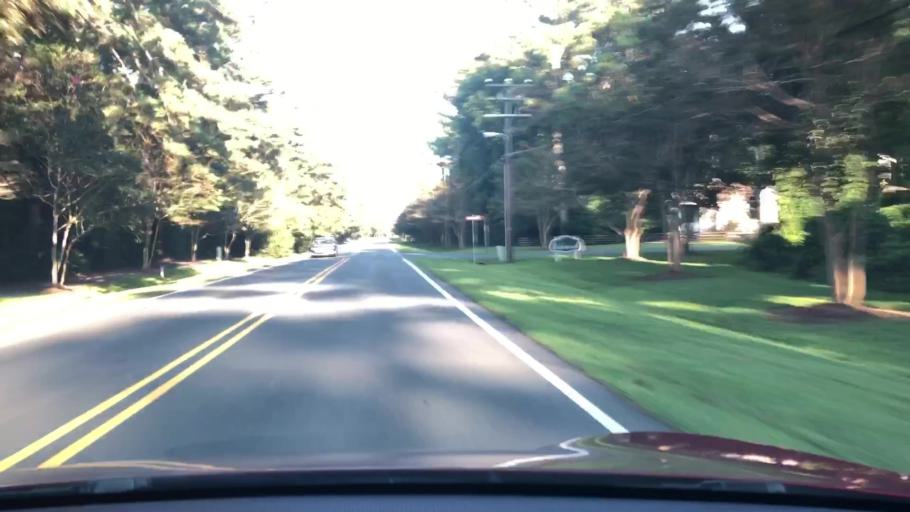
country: US
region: North Carolina
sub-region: Dare County
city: Manteo
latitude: 35.9334
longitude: -75.6970
